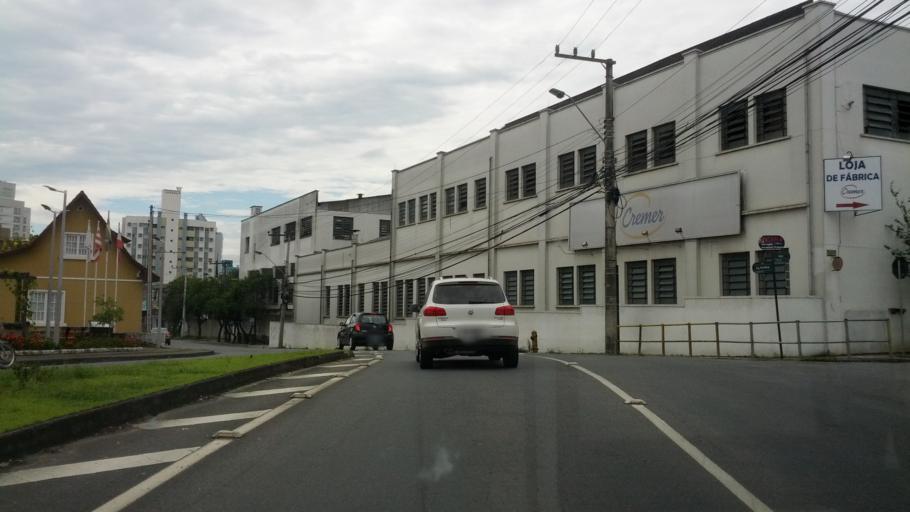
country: BR
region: Santa Catarina
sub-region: Blumenau
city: Blumenau
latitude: -26.9002
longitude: -49.0795
